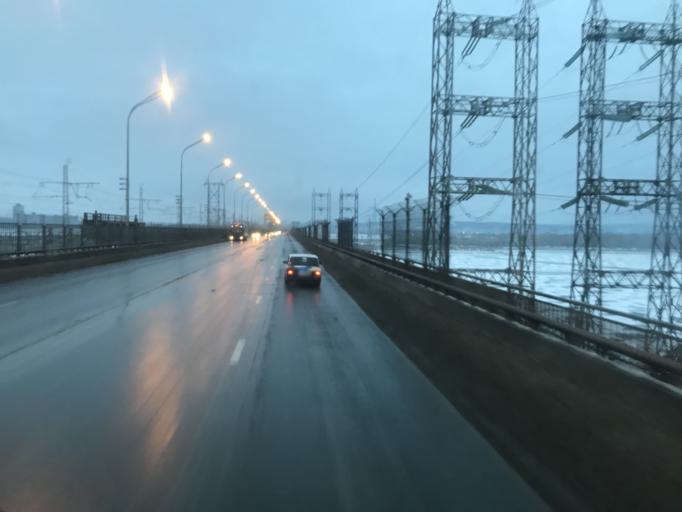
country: RU
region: Samara
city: Zhigulevsk
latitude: 53.4547
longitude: 49.4941
